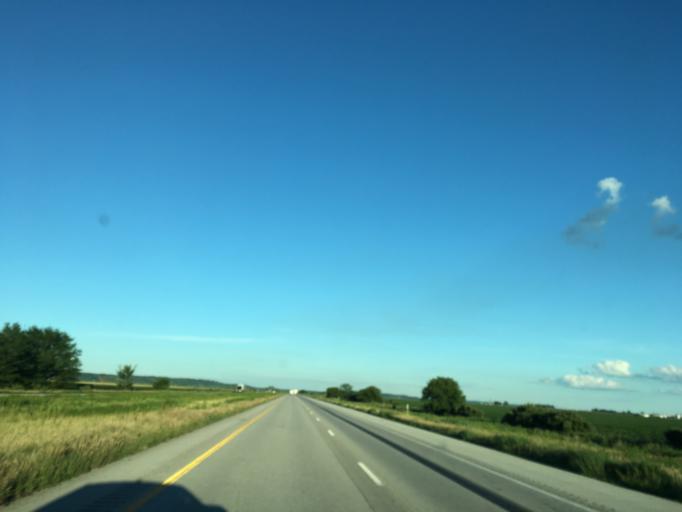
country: US
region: Iowa
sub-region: Fremont County
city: Hamburg
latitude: 40.6395
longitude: -95.7361
